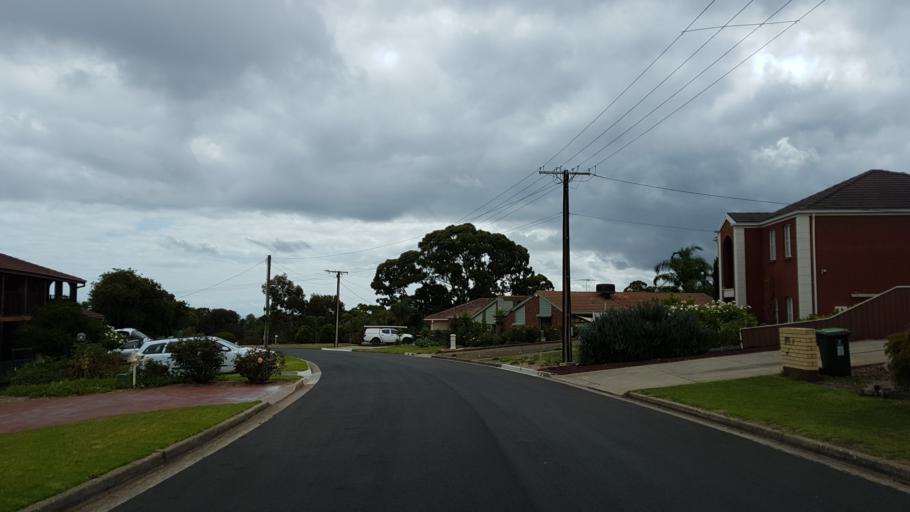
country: AU
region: South Australia
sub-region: Onkaparinga
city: Bedford Park
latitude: -35.0450
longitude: 138.5697
